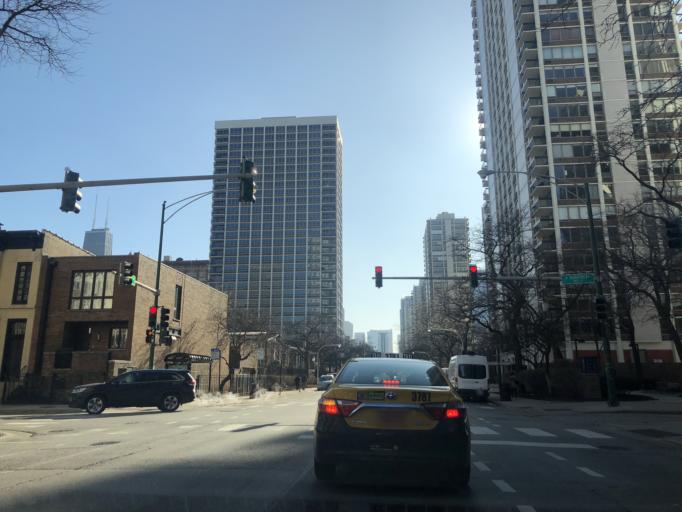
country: US
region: Illinois
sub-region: Cook County
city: Chicago
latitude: 41.9097
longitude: -87.6317
